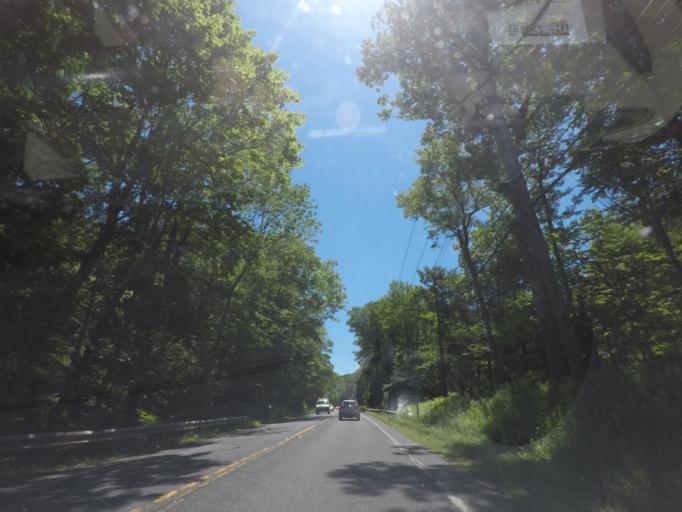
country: US
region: Massachusetts
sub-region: Berkshire County
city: Becket
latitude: 42.2738
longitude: -73.1419
